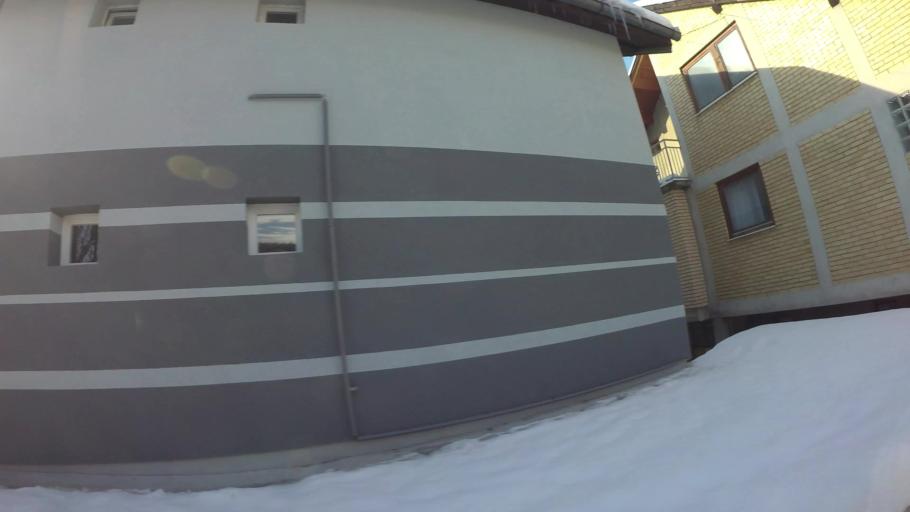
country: BA
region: Federation of Bosnia and Herzegovina
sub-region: Kanton Sarajevo
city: Sarajevo
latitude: 43.8405
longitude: 18.3632
